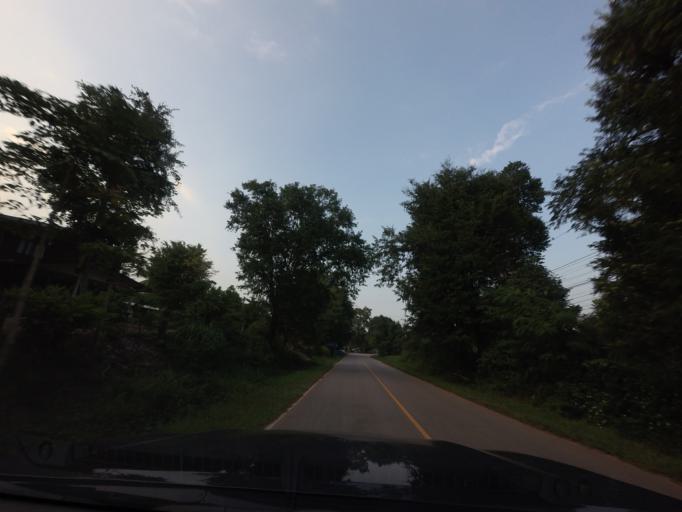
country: TH
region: Loei
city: Na Haeo
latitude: 17.4440
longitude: 101.0553
